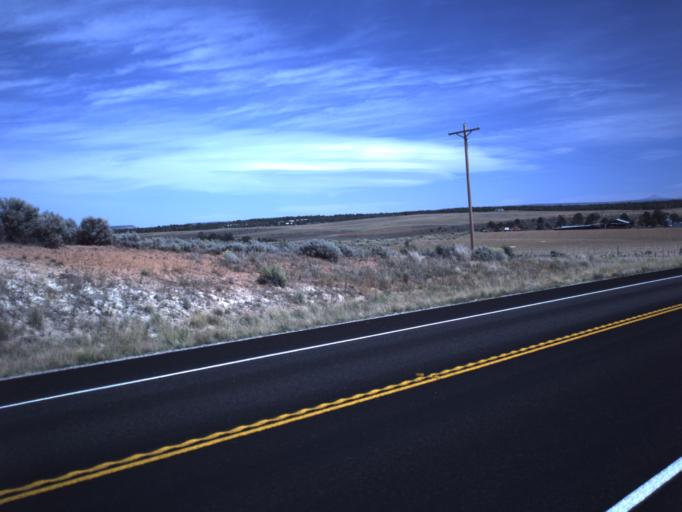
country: US
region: Utah
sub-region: San Juan County
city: Monticello
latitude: 37.8649
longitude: -109.2290
